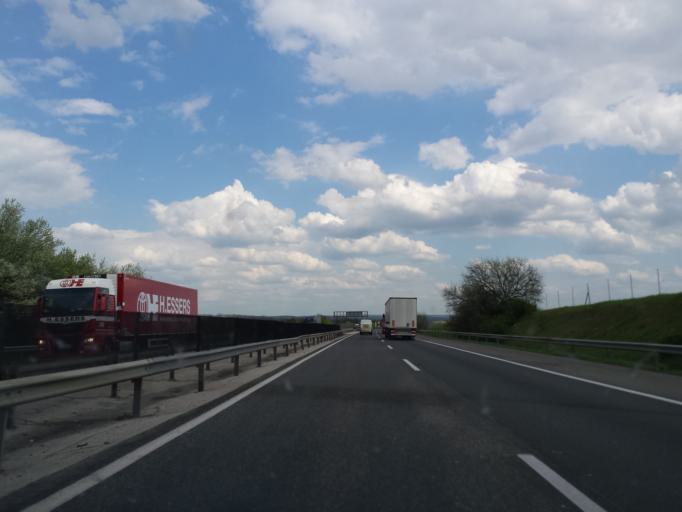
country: HU
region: Pest
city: Zsambek
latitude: 47.5110
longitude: 18.7272
